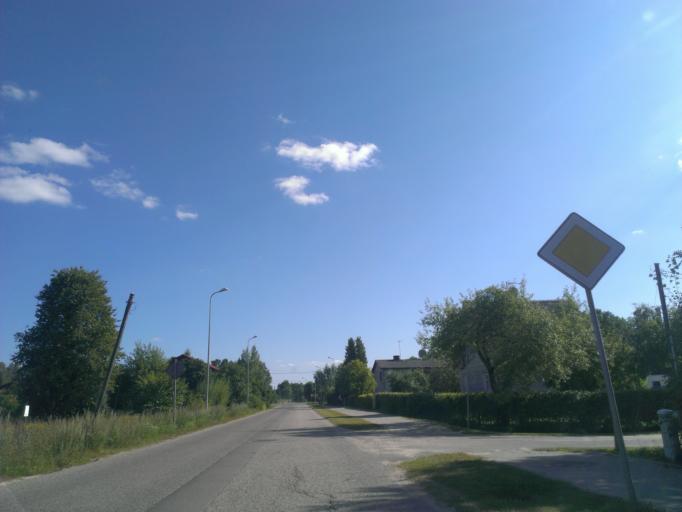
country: LV
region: Sigulda
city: Sigulda
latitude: 57.1608
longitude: 24.8883
